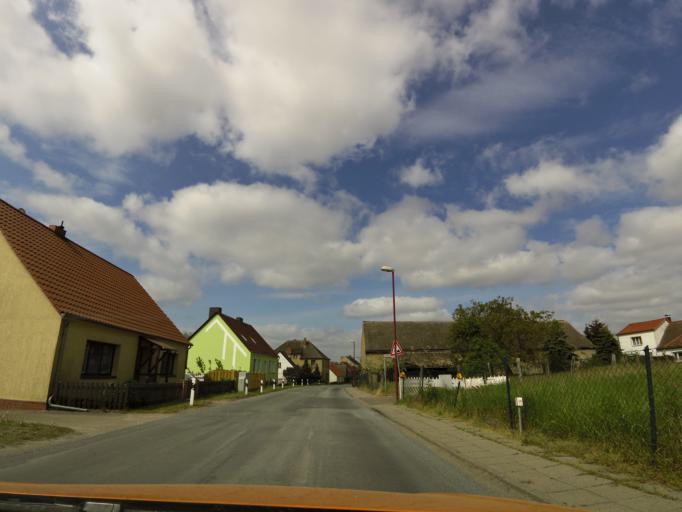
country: DE
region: Brandenburg
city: Wiesenburg
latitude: 52.1082
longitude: 12.3987
